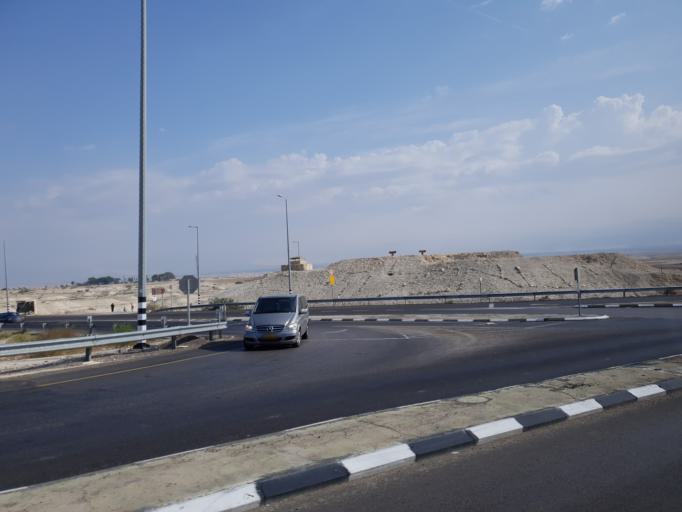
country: PS
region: West Bank
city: Jericho
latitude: 31.7997
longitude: 35.4901
